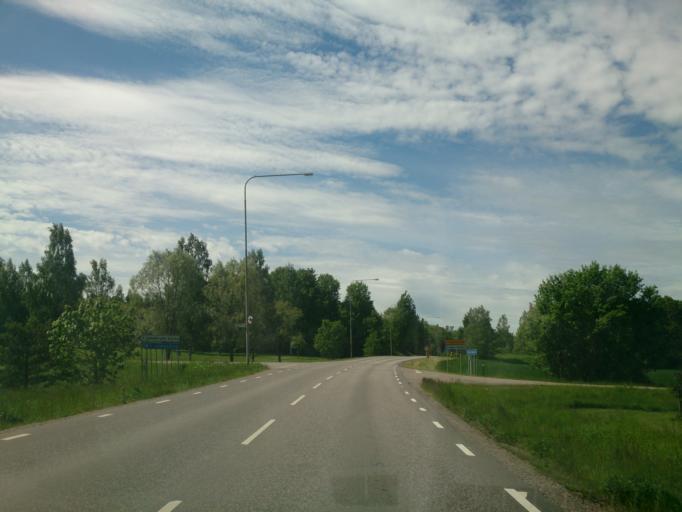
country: SE
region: OEstergoetland
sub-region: Linkopings Kommun
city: Sturefors
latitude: 58.3782
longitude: 15.7217
